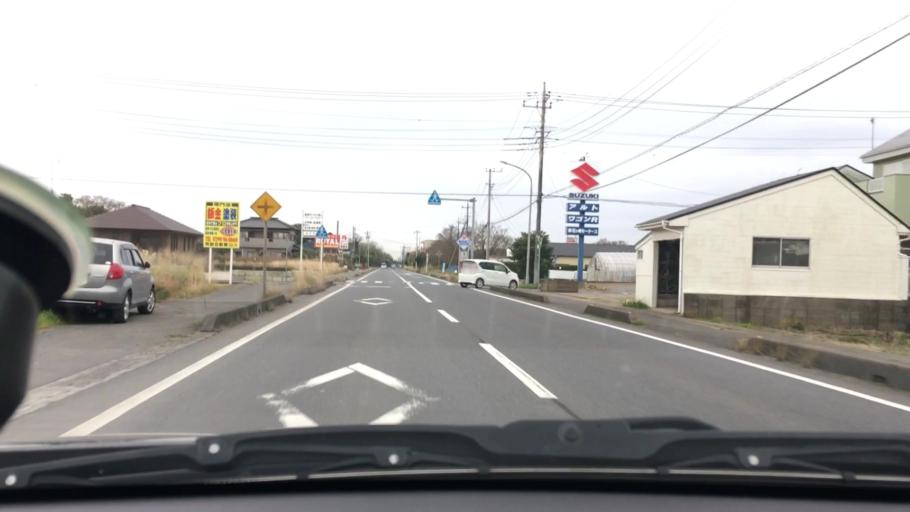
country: JP
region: Chiba
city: Omigawa
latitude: 35.8677
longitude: 140.6634
